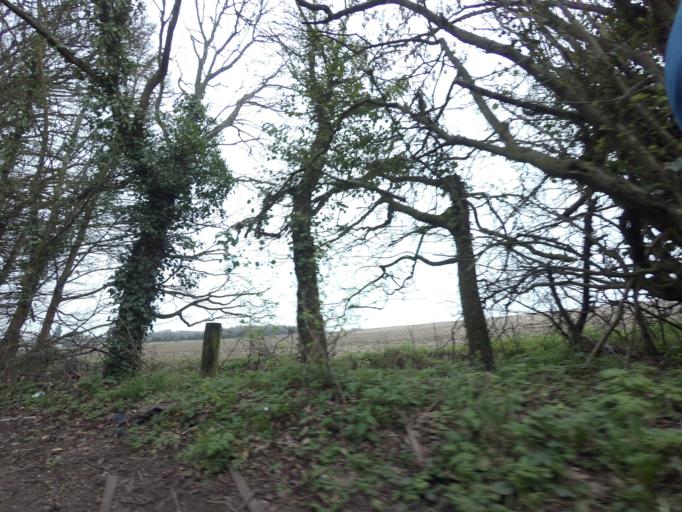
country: GB
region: England
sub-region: Kent
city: Swanley
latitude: 51.3727
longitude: 0.1577
